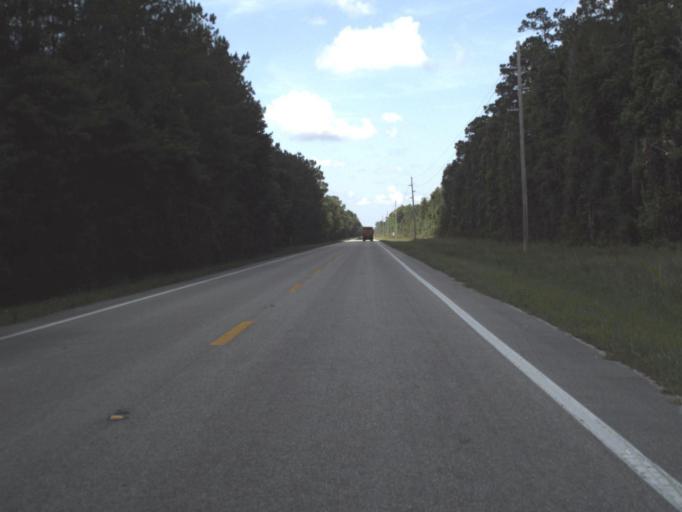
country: US
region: Florida
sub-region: Levy County
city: Bronson
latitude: 29.3688
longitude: -82.7220
